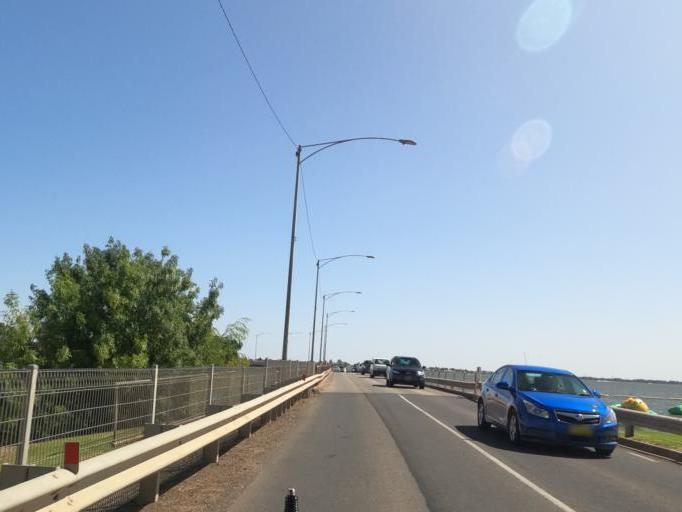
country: AU
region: Victoria
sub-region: Moira
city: Yarrawonga
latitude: -36.0076
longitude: 146.0048
